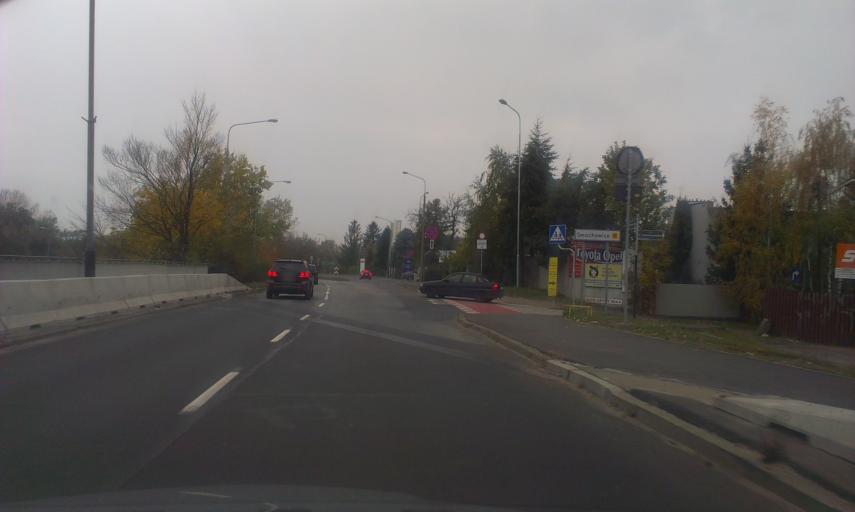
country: PL
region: Greater Poland Voivodeship
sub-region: Powiat poznanski
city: Suchy Las
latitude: 52.4304
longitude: 16.8446
